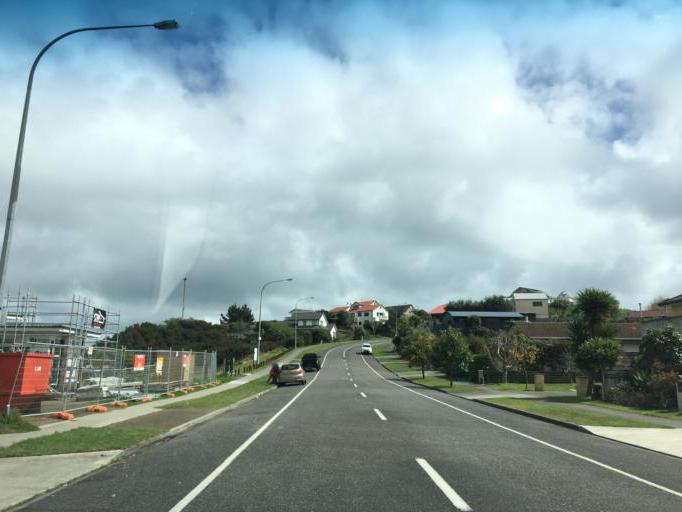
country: NZ
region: Wellington
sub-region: Kapiti Coast District
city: Paraparaumu
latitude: -40.8761
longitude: 175.0156
